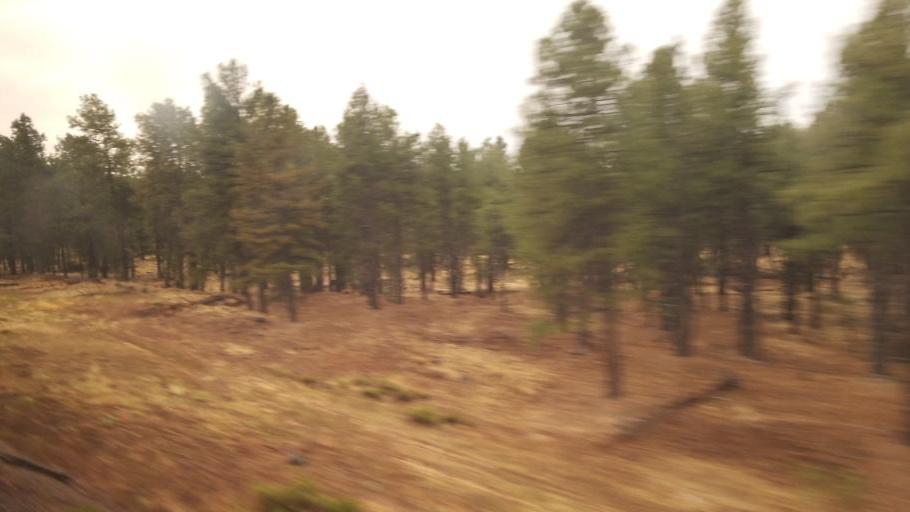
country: US
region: Arizona
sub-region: Coconino County
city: Parks
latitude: 35.2537
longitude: -111.9171
